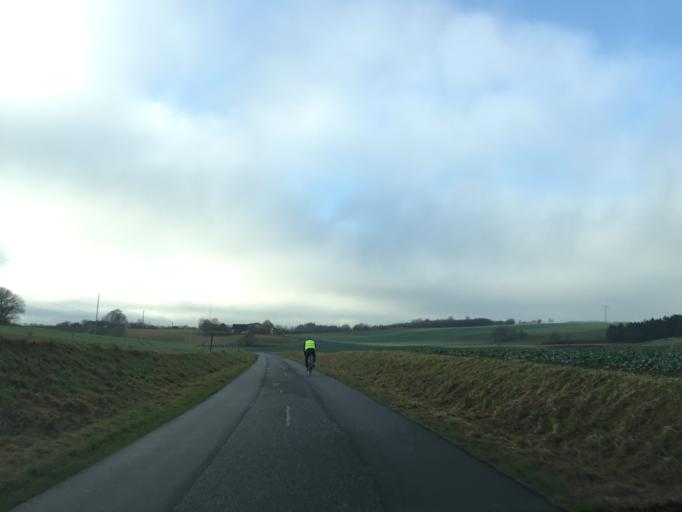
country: DK
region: Central Jutland
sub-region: Skanderborg Kommune
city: Ry
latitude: 56.1682
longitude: 9.7798
